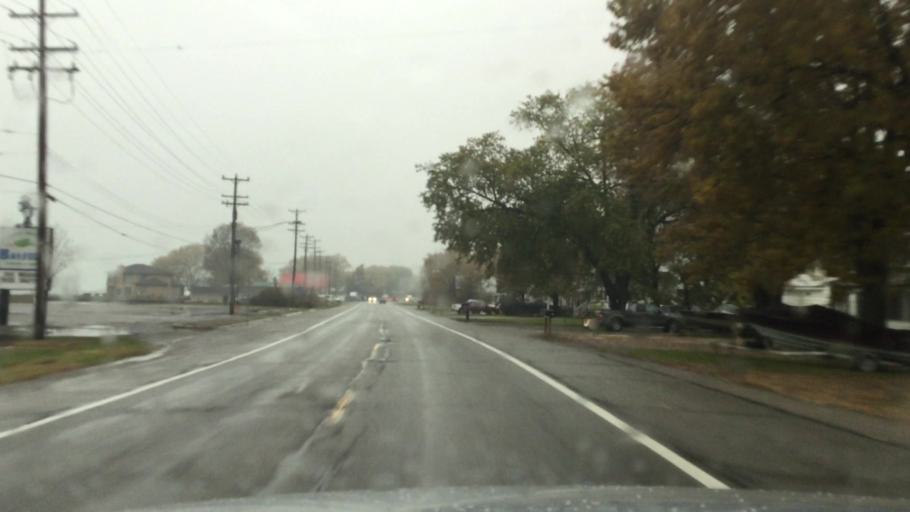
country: US
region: Michigan
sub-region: Saint Clair County
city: Pearl Beach
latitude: 42.6764
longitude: -82.6371
